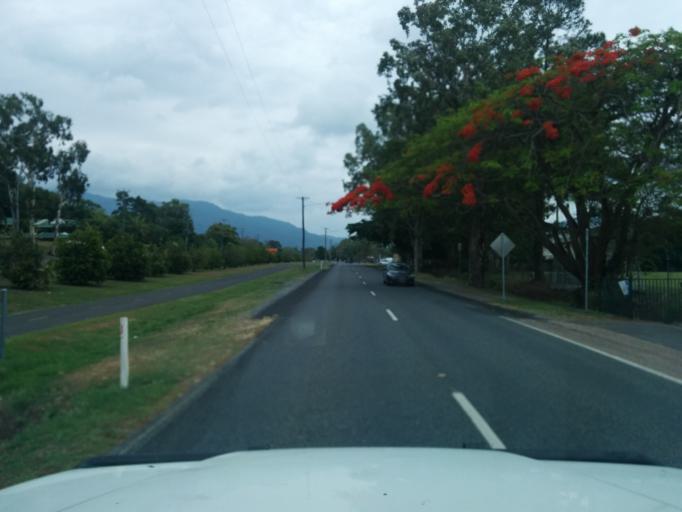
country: AU
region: Queensland
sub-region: Cairns
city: Redlynch
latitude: -16.8746
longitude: 145.7388
